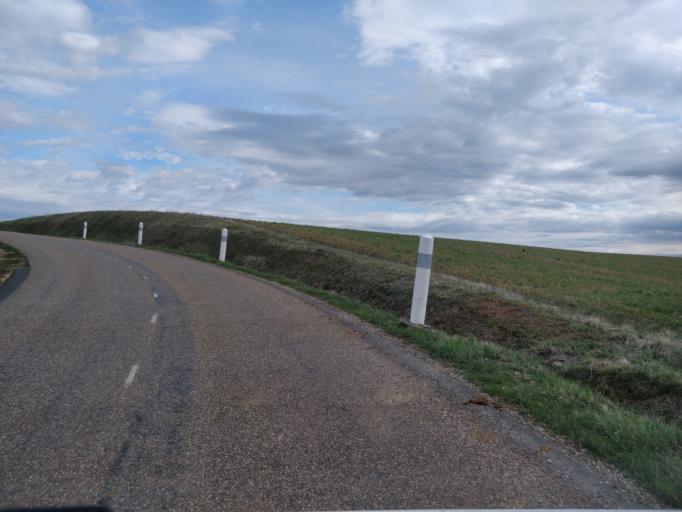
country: FR
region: Lorraine
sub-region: Departement de Meurthe-et-Moselle
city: Doncourt-les-Conflans
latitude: 49.1105
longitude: 5.9042
